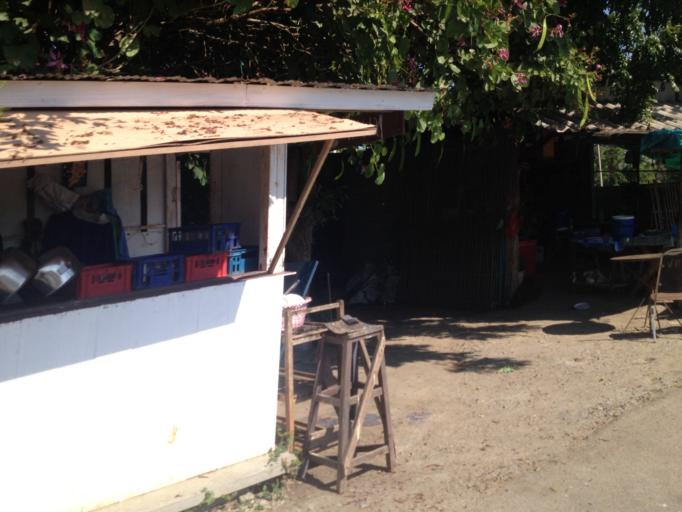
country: TH
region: Chiang Mai
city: Hang Dong
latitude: 18.7013
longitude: 98.9225
